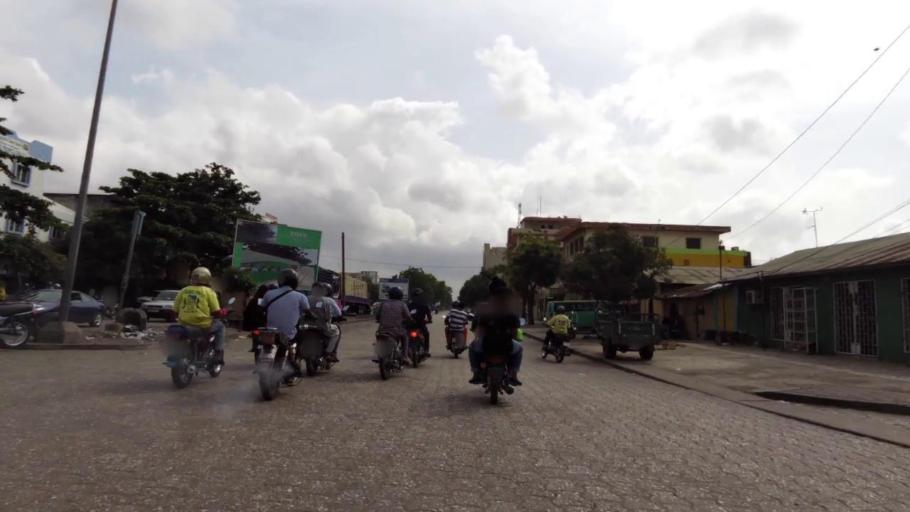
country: BJ
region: Littoral
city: Cotonou
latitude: 6.3578
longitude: 2.4266
